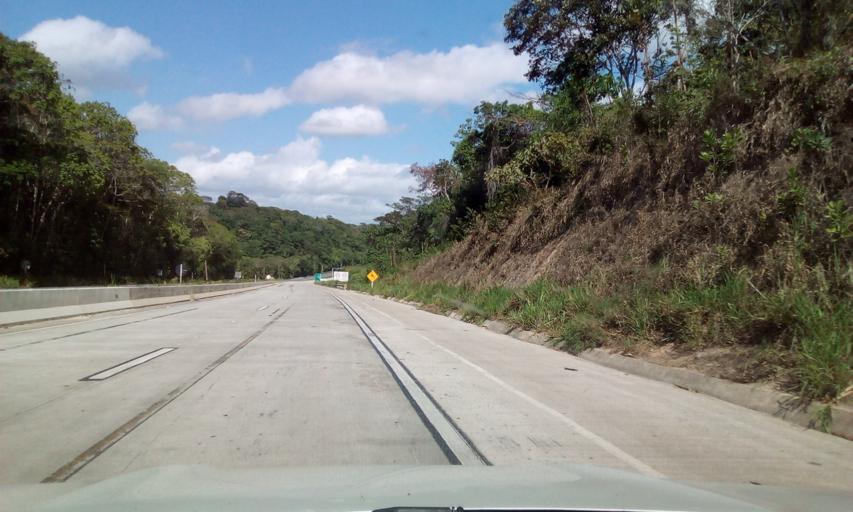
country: BR
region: Alagoas
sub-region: Rio Largo
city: Rio Largo
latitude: -9.5050
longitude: -35.9208
